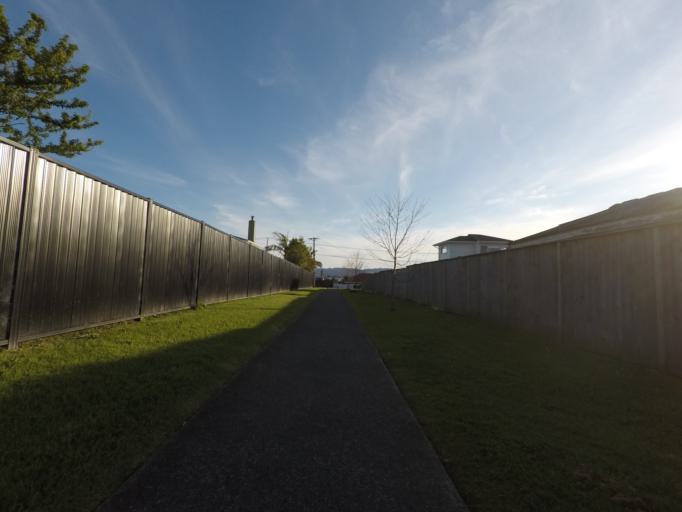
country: NZ
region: Auckland
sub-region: Auckland
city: Rosebank
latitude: -36.8403
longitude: 174.6444
